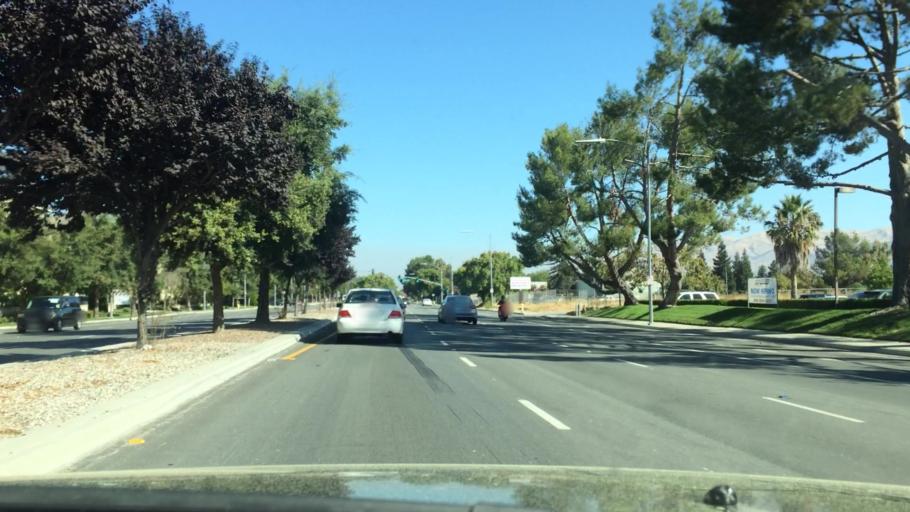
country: US
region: California
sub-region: Santa Clara County
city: Milpitas
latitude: 37.3950
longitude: -121.9018
